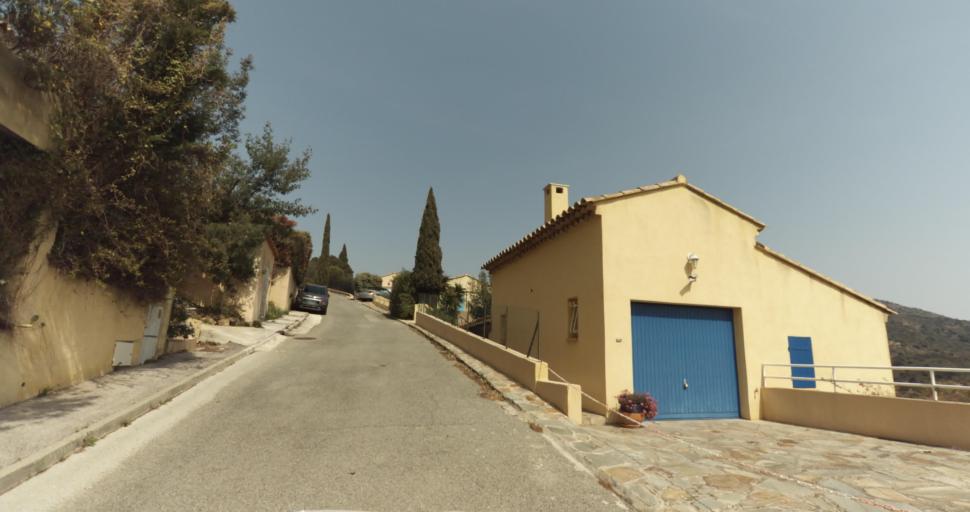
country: FR
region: Provence-Alpes-Cote d'Azur
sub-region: Departement du Var
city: Bormes-les-Mimosas
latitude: 43.1491
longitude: 6.3480
